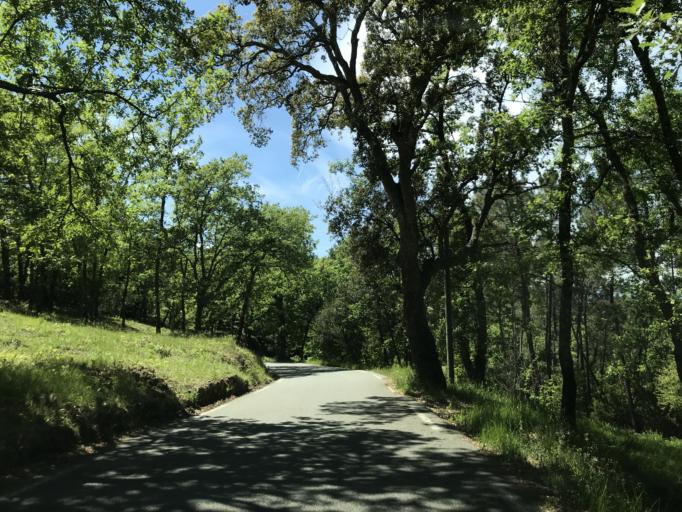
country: FR
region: Provence-Alpes-Cote d'Azur
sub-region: Departement du Var
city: Tanneron
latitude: 43.5824
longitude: 6.8326
